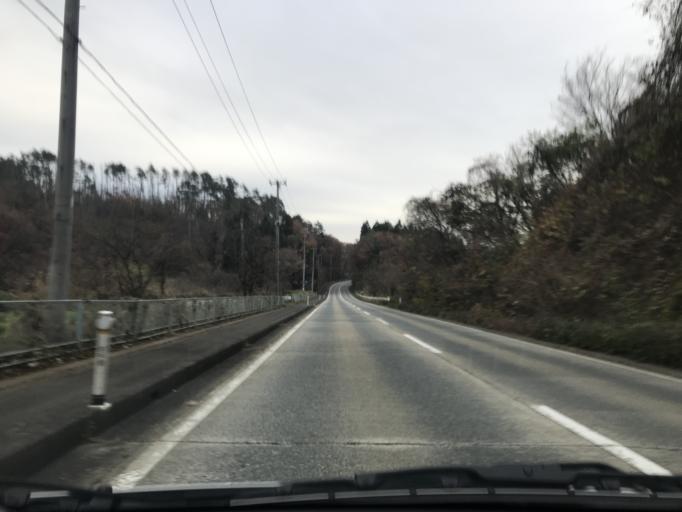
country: JP
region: Iwate
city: Kitakami
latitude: 39.2963
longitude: 141.2100
